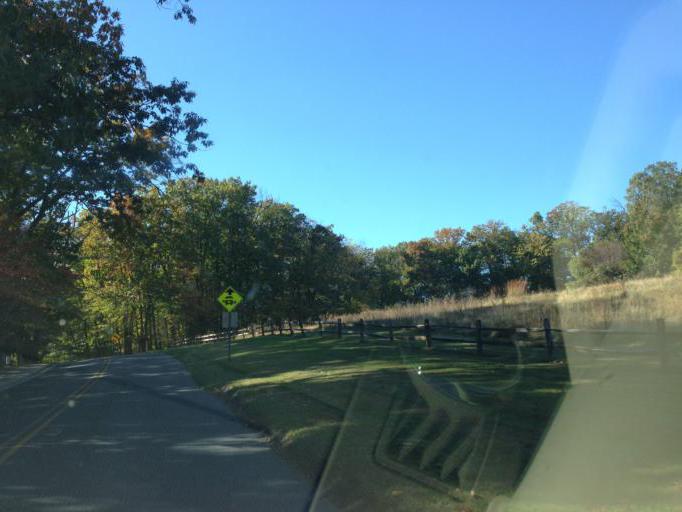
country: US
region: Maryland
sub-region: Montgomery County
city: Germantown
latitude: 39.1975
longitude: -77.2347
